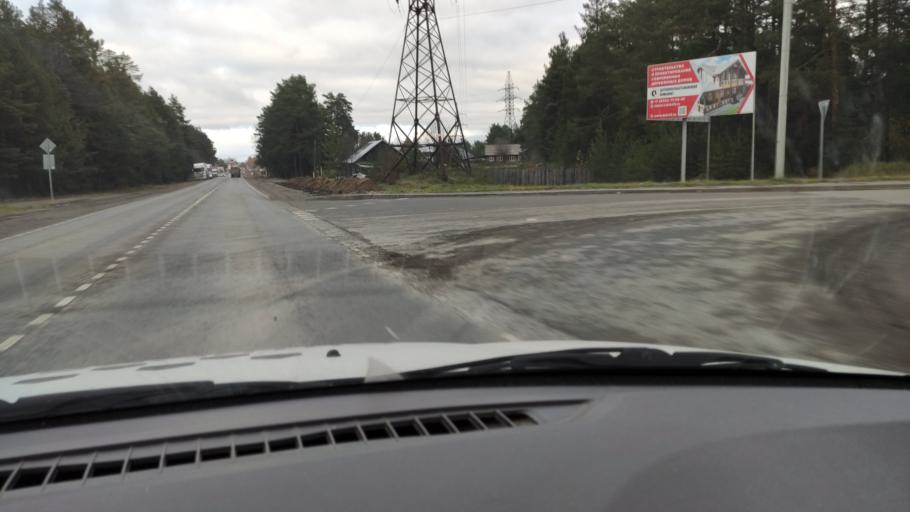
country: RU
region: Kirov
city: Belaya Kholunitsa
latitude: 58.8459
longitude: 50.8170
